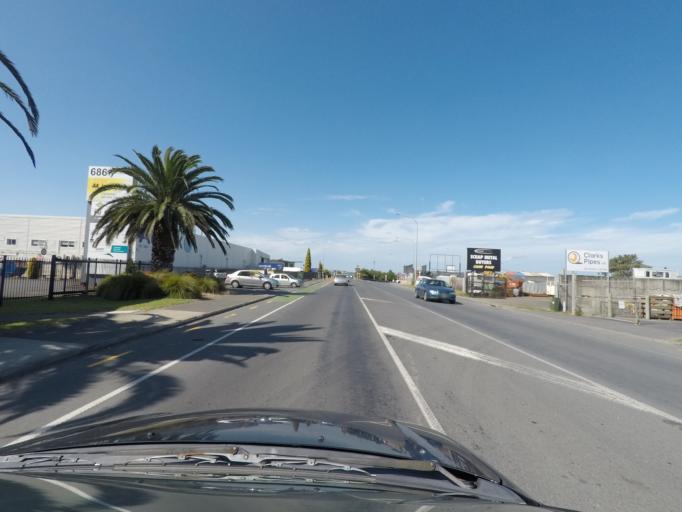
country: NZ
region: Auckland
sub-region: Auckland
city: Rosebank
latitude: -36.8709
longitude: 174.6717
